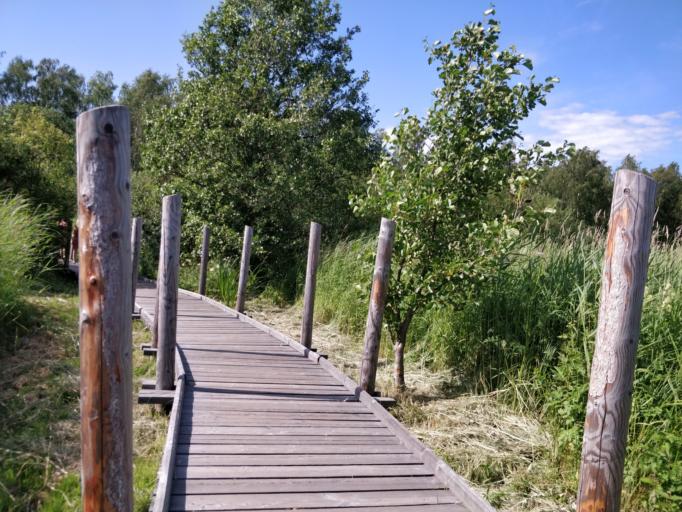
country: FI
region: Uusimaa
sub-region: Helsinki
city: Helsinki
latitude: 60.2121
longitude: 24.9894
